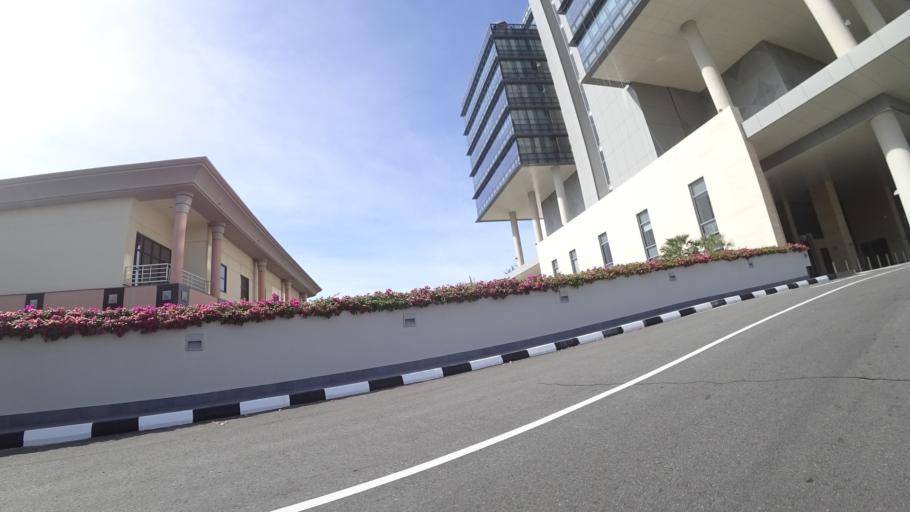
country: BN
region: Brunei and Muara
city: Bandar Seri Begawan
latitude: 4.9495
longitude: 114.8313
